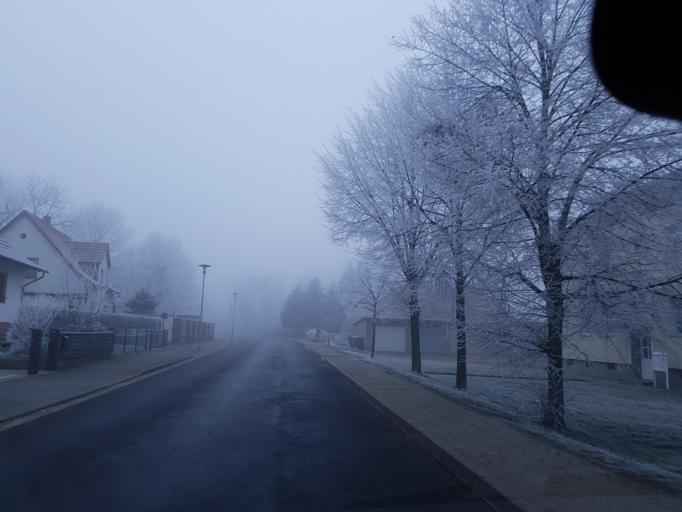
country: DE
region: Brandenburg
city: Muhlberg
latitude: 51.4627
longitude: 13.2243
